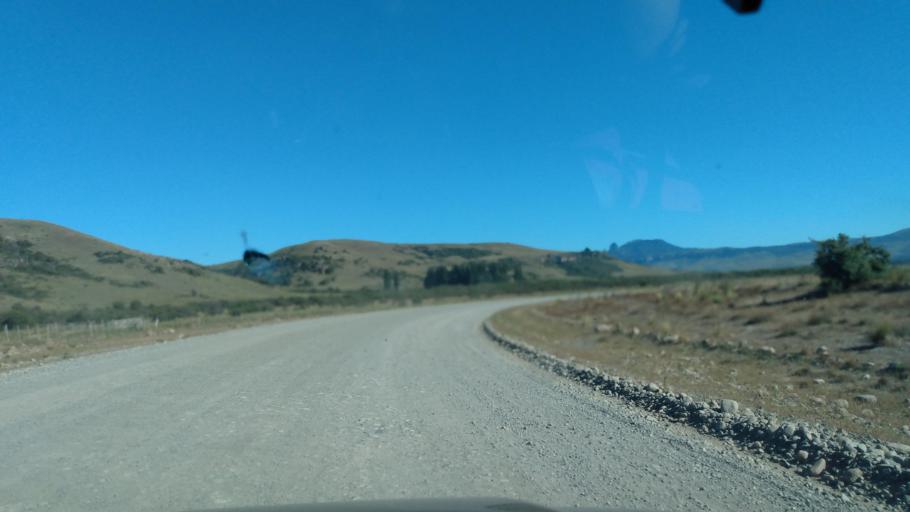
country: AR
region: Neuquen
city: Junin de los Andes
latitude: -39.8572
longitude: -71.1879
